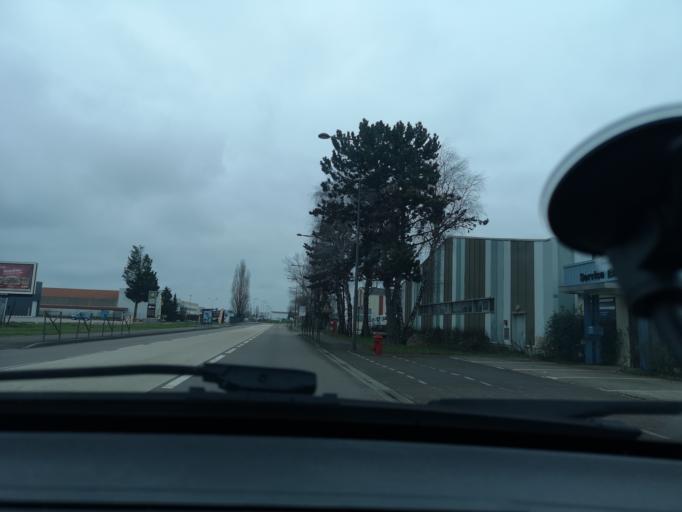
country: FR
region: Bourgogne
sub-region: Departement de Saone-et-Loire
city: Virey-le-Grand
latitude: 46.8148
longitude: 4.8577
